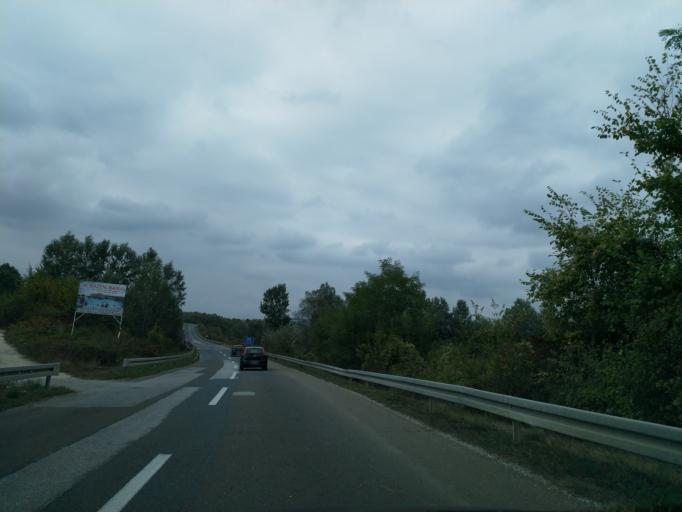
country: RS
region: Central Serbia
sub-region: Sumadijski Okrug
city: Topola
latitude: 44.2377
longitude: 20.7105
